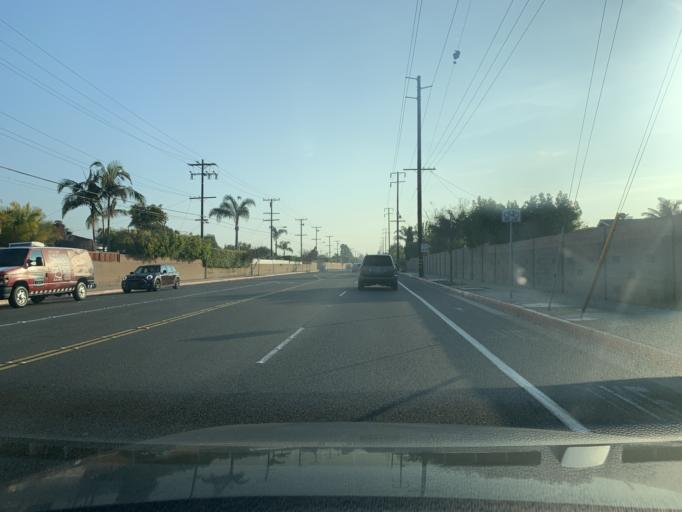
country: US
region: California
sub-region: Orange County
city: Westminster
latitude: 33.7372
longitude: -118.0240
